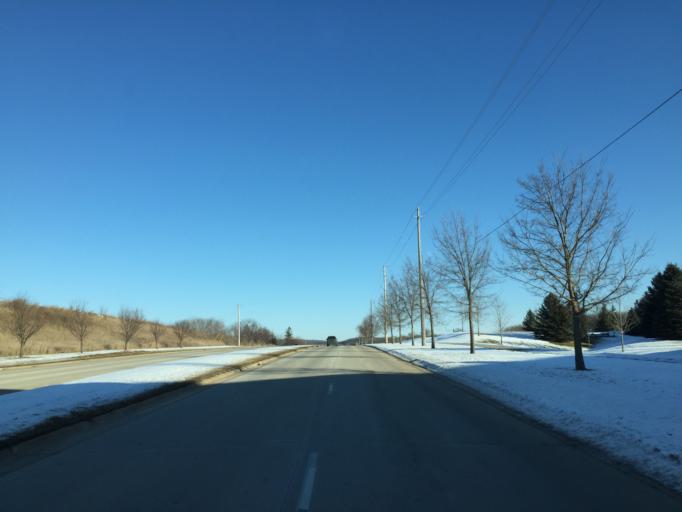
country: US
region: Minnesota
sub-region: Olmsted County
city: Rochester
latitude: 44.0796
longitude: -92.4841
